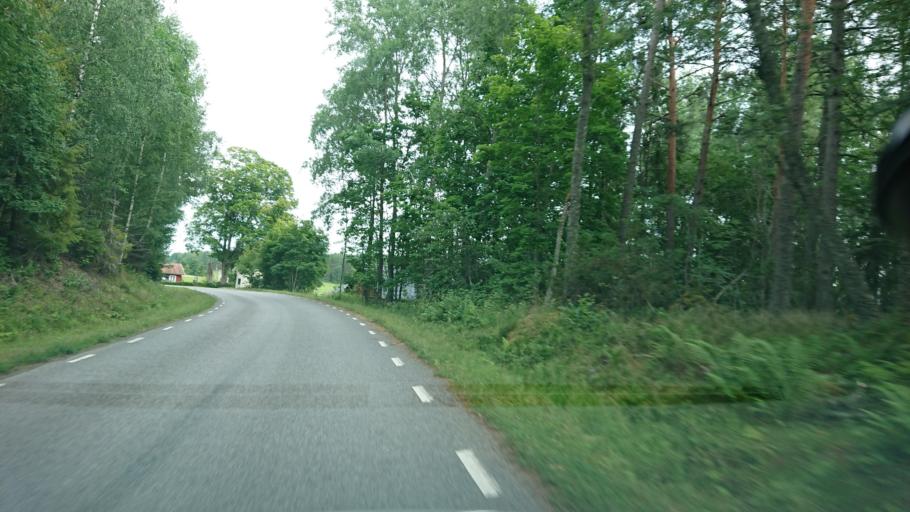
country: SE
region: Uppsala
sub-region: Osthammars Kommun
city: Bjorklinge
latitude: 60.0039
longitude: 17.4545
